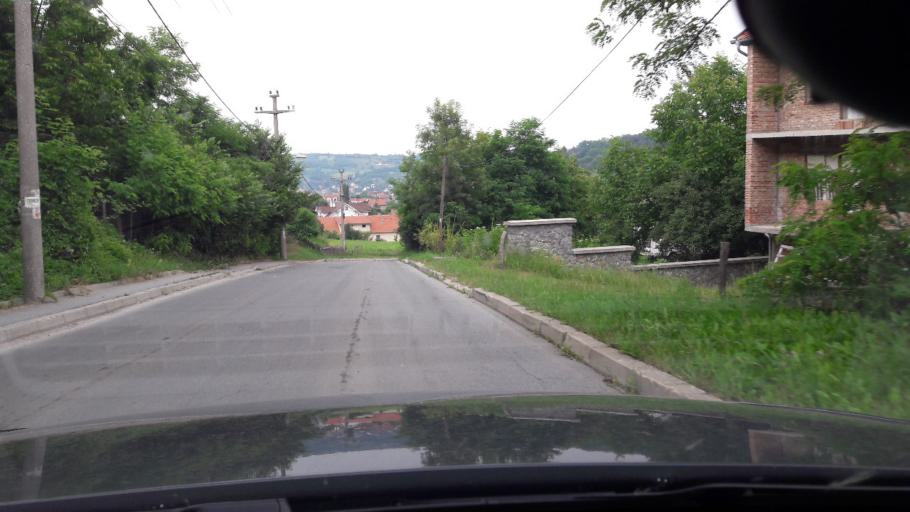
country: RS
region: Central Serbia
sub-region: Belgrade
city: Grocka
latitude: 44.6589
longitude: 20.5920
